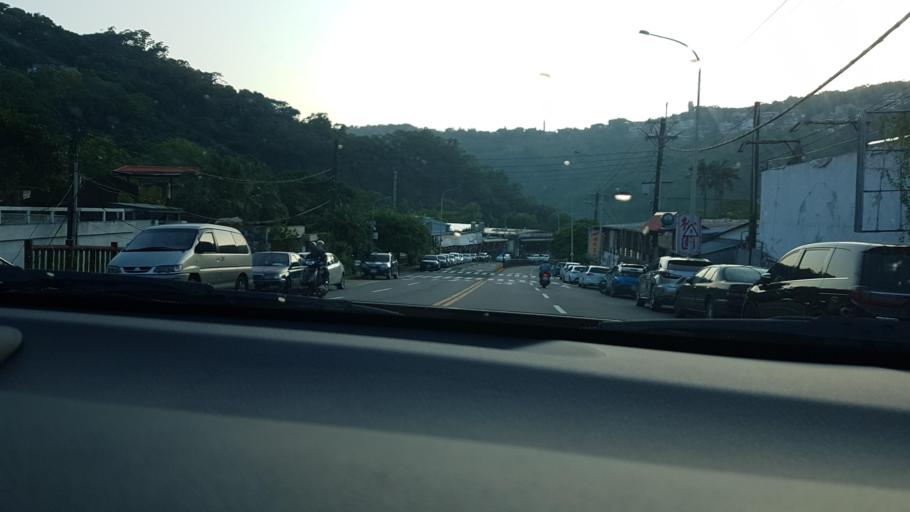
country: TW
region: Taipei
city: Taipei
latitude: 25.1126
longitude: 121.5634
